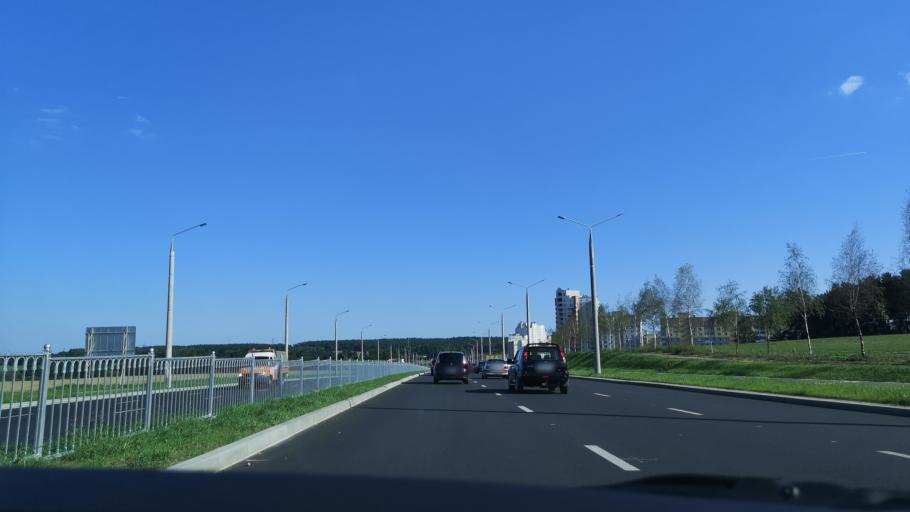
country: BY
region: Grodnenskaya
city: Hrodna
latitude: 53.6492
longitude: 23.8616
